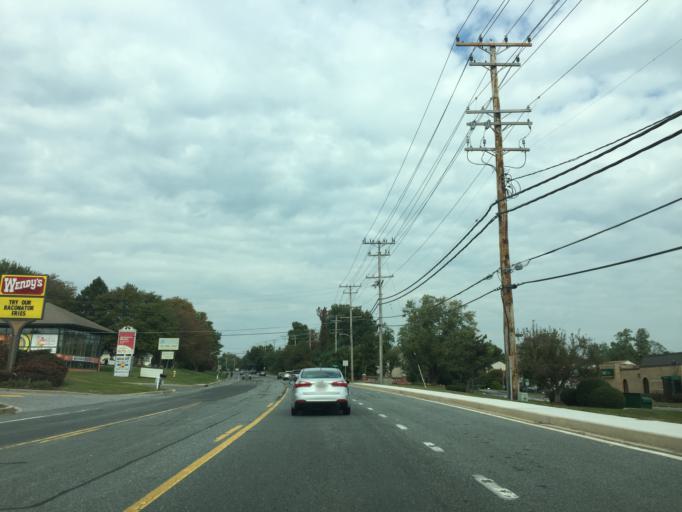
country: US
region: Maryland
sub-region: Harford County
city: Bel Air South
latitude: 39.4793
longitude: -76.3105
